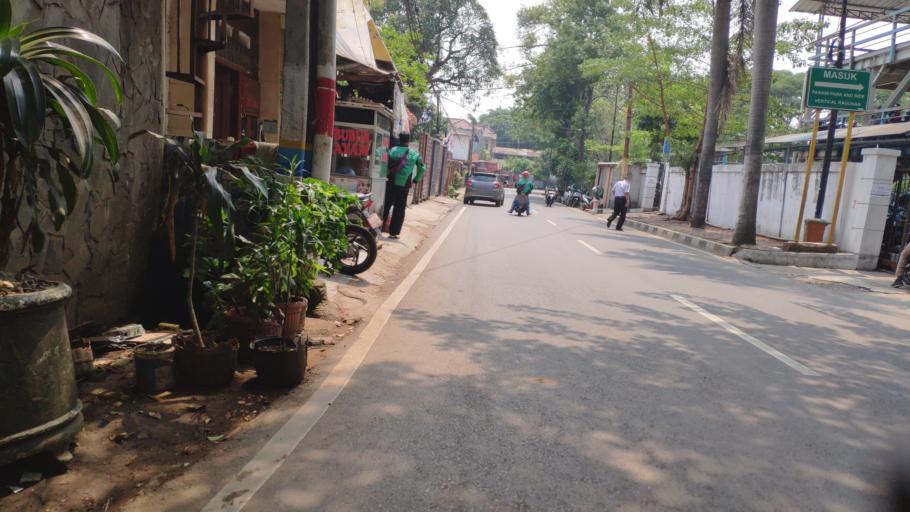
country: ID
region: West Java
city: Pamulang
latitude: -6.3052
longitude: 106.8182
